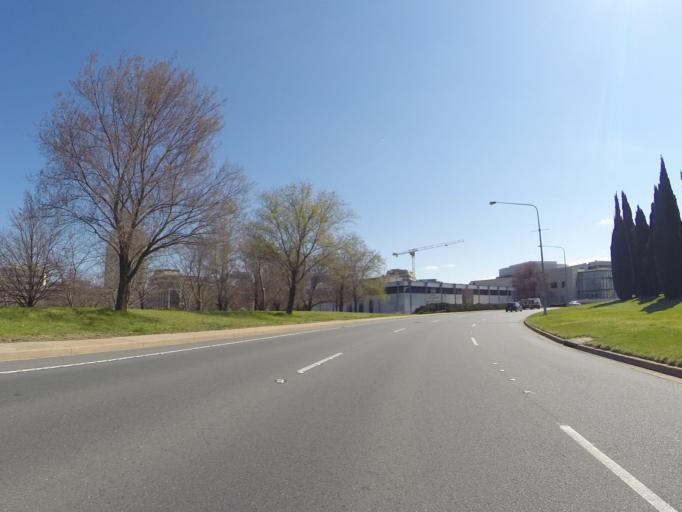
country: AU
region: Australian Capital Territory
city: Canberra
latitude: -35.2823
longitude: 149.1274
